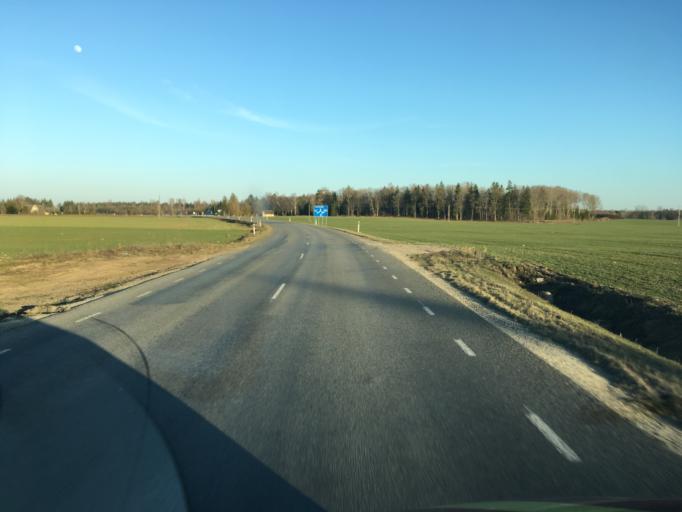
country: EE
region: Raplamaa
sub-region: Kehtna vald
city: Kehtna
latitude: 59.0575
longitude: 24.9437
